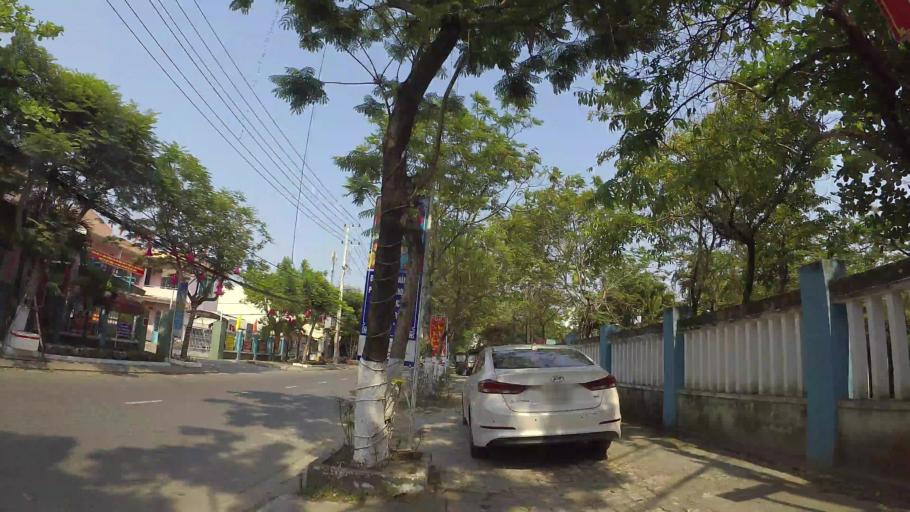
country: VN
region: Da Nang
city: Cam Le
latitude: 16.0103
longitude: 108.1945
